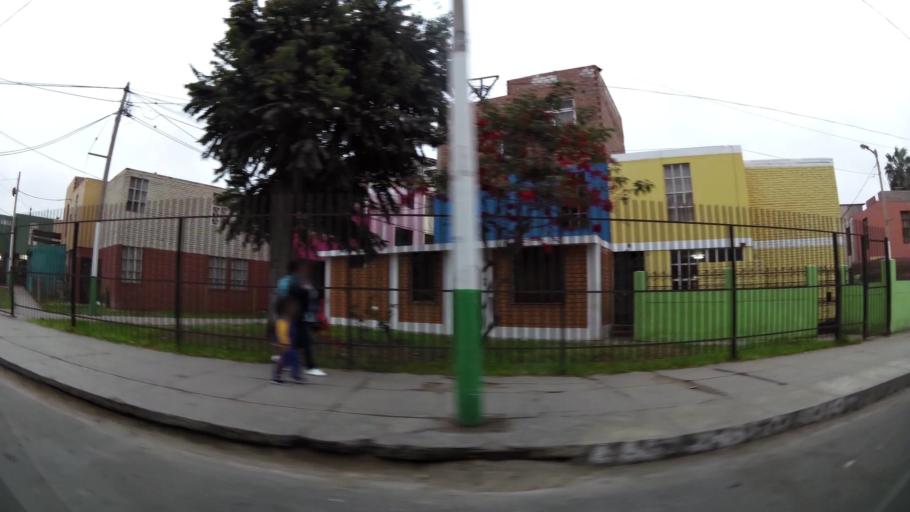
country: PE
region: Callao
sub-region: Callao
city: Callao
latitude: -12.0676
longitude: -77.1255
